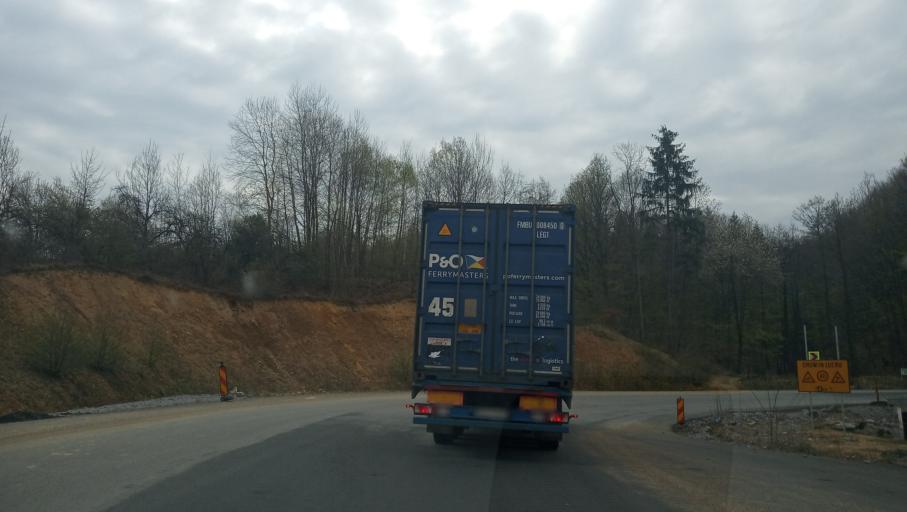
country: RO
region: Bihor
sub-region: Comuna Cristioru de Jos
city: Cristioru de Jos
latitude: 46.4150
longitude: 22.5385
